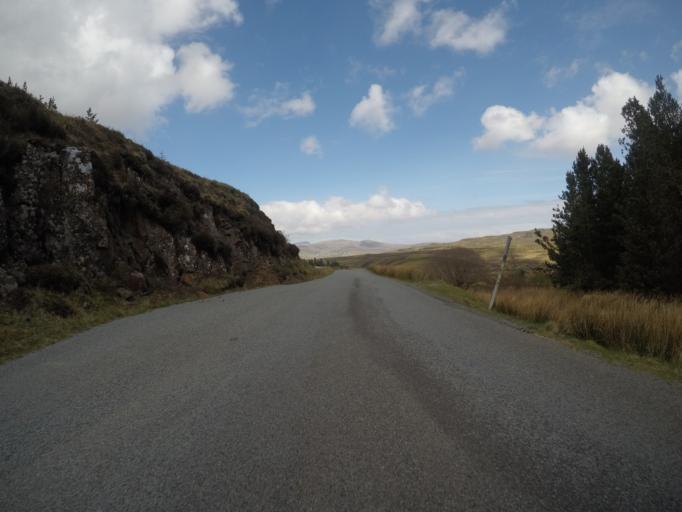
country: GB
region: Scotland
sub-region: Highland
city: Isle of Skye
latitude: 57.4101
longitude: -6.3042
